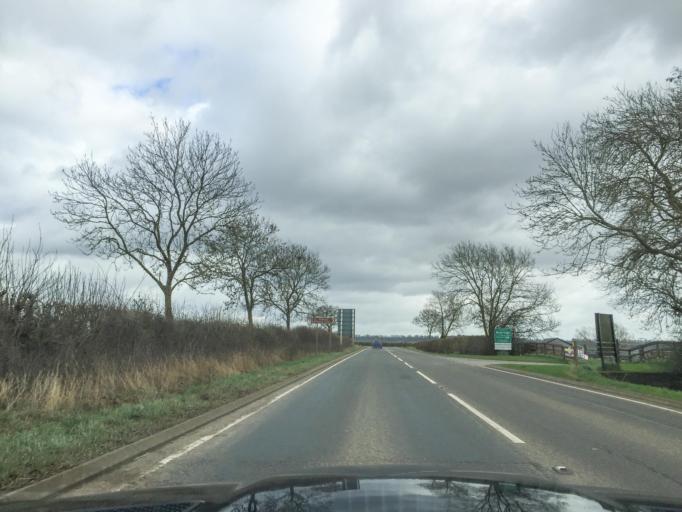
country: GB
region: England
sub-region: Warwickshire
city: Wellesbourne Mountford
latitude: 52.1229
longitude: -1.5284
